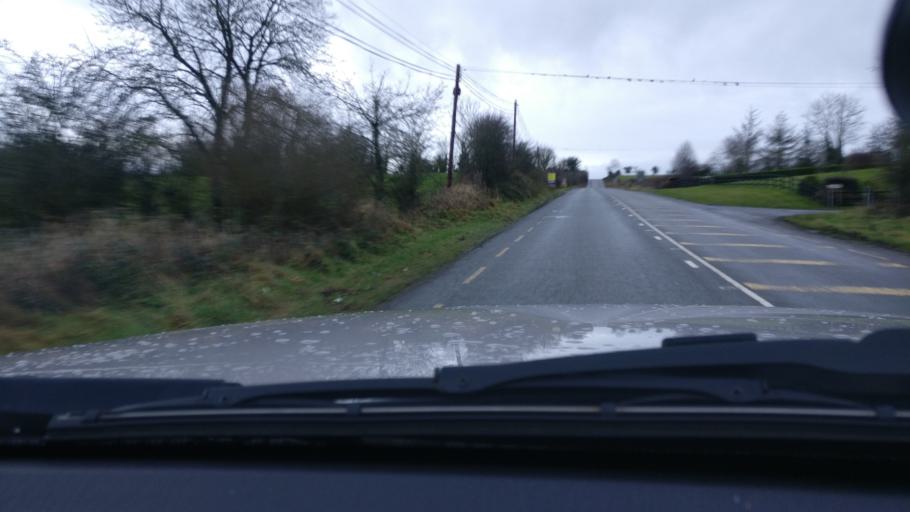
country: IE
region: Ulster
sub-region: An Cabhan
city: Ballyjamesduff
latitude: 53.8562
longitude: -7.2329
